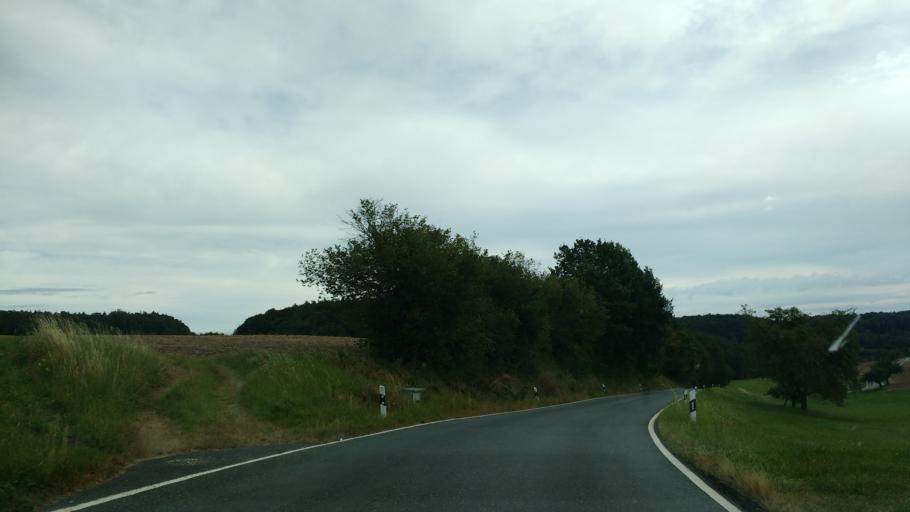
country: DE
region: Bavaria
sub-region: Regierungsbezirk Unterfranken
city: Geiselwind
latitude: 49.7984
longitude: 10.4923
